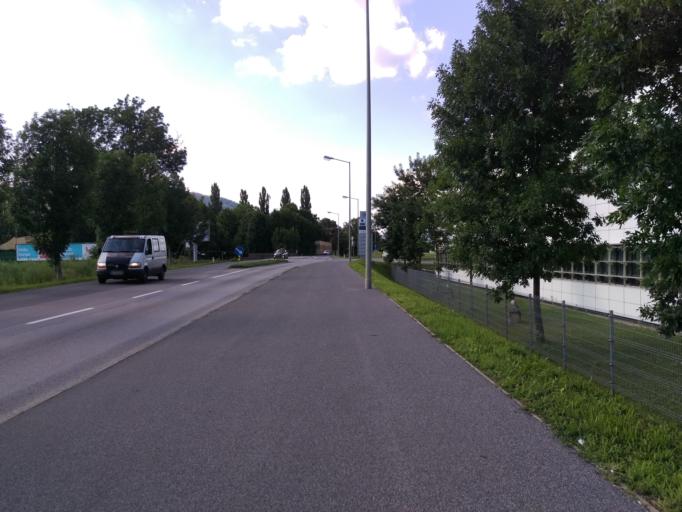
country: AT
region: Styria
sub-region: Graz Stadt
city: Wetzelsdorf
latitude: 47.0611
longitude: 15.4135
